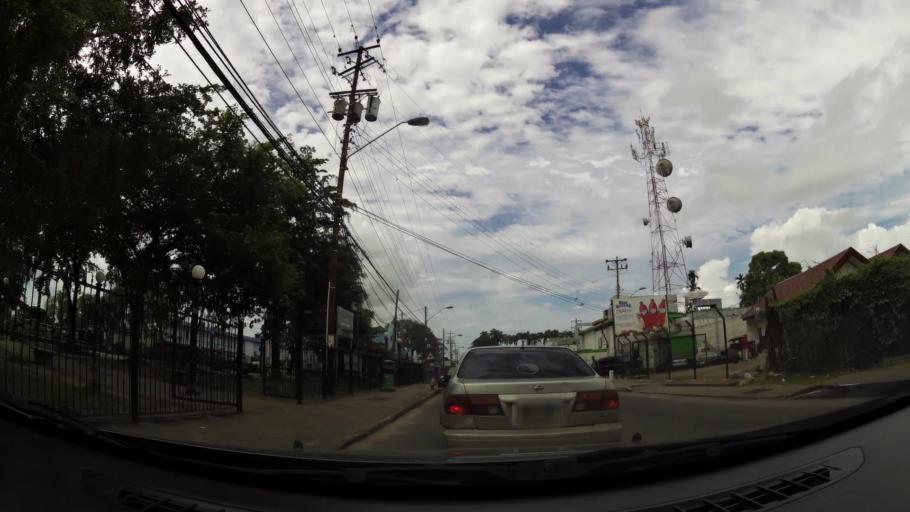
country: TT
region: Couva-Tabaquite-Talparo
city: Couva
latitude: 10.4219
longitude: -61.4594
